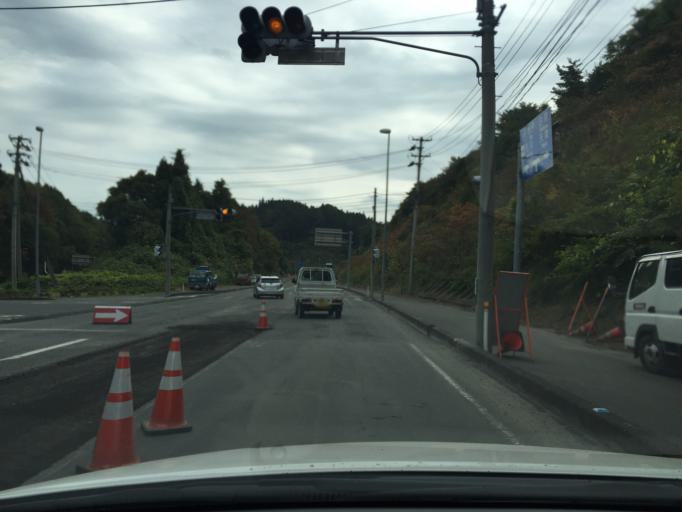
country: JP
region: Fukushima
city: Ishikawa
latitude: 37.0462
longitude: 140.3743
